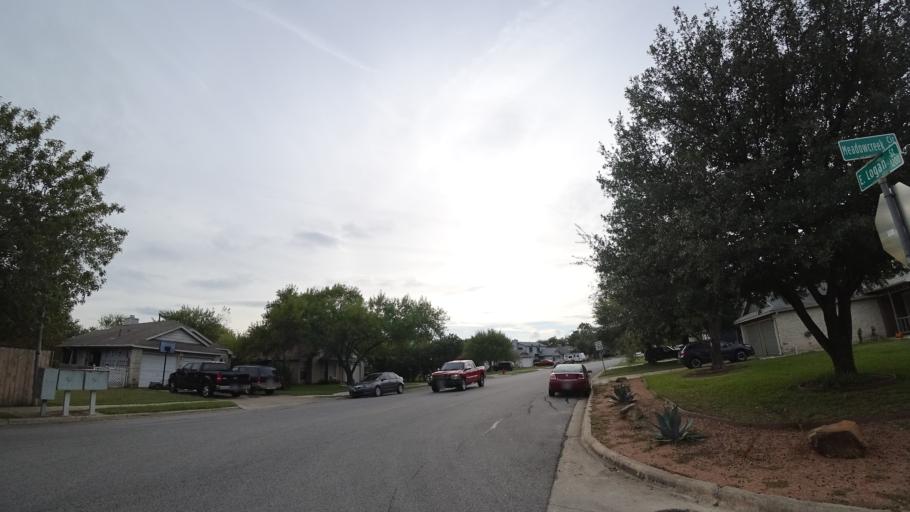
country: US
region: Texas
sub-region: Williamson County
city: Round Rock
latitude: 30.5027
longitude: -97.6657
